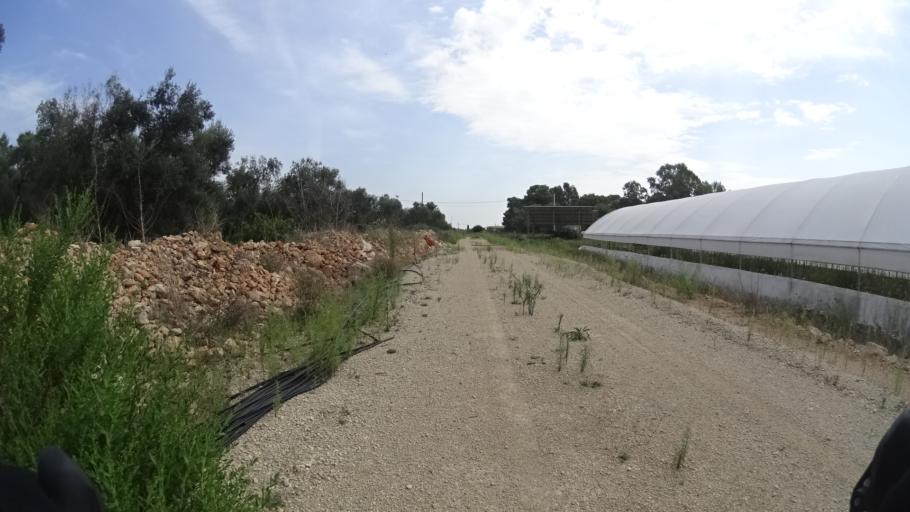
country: IT
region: Apulia
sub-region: Provincia di Lecce
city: Porto Cesareo
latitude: 40.2763
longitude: 17.9334
